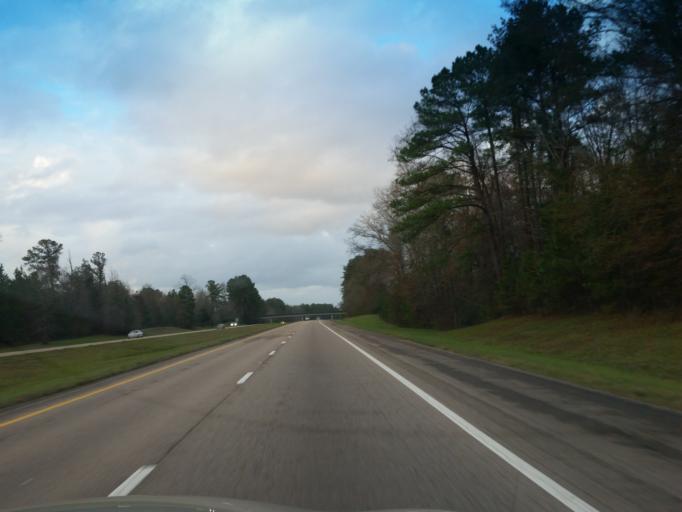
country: US
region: Mississippi
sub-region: Clarke County
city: Stonewall
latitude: 32.0338
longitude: -88.9216
